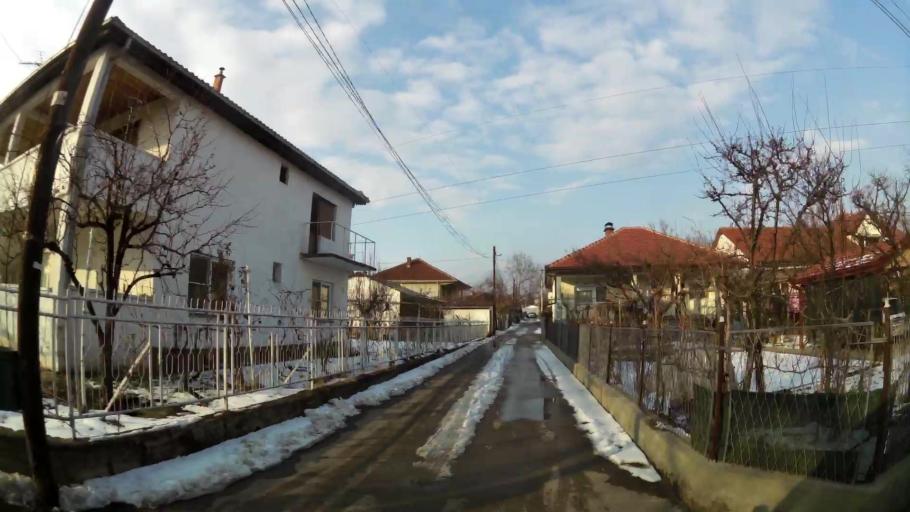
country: MK
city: Creshevo
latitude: 42.0295
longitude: 21.5195
